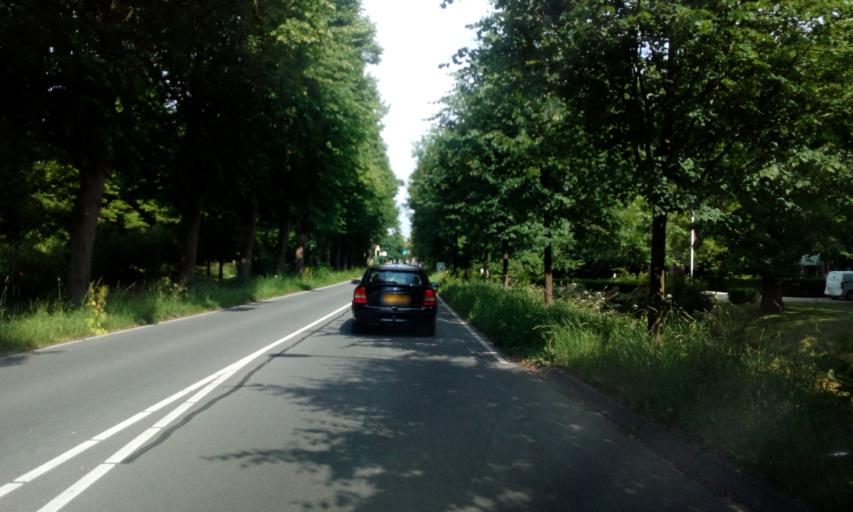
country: NL
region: Utrecht
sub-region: Stichtse Vecht
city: Breukelen
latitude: 52.1680
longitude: 5.0066
